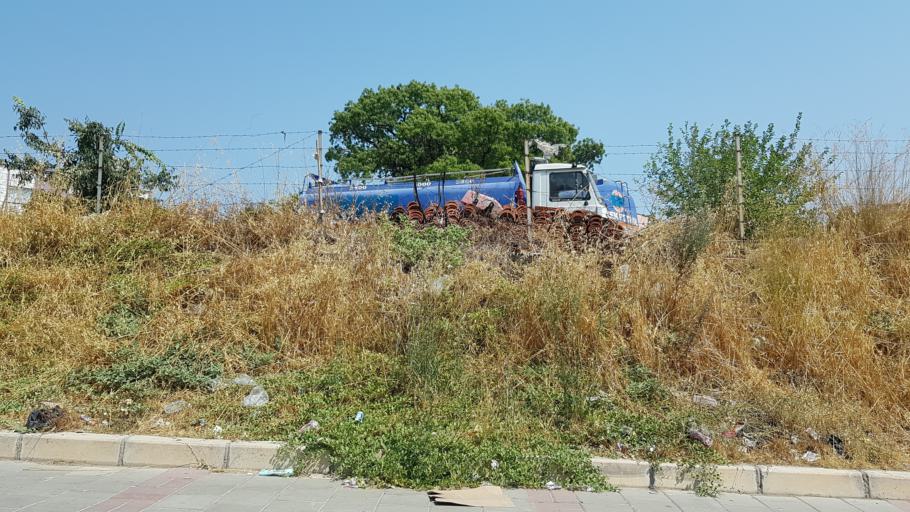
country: TR
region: Izmir
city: Karabaglar
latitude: 38.3791
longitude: 27.1125
